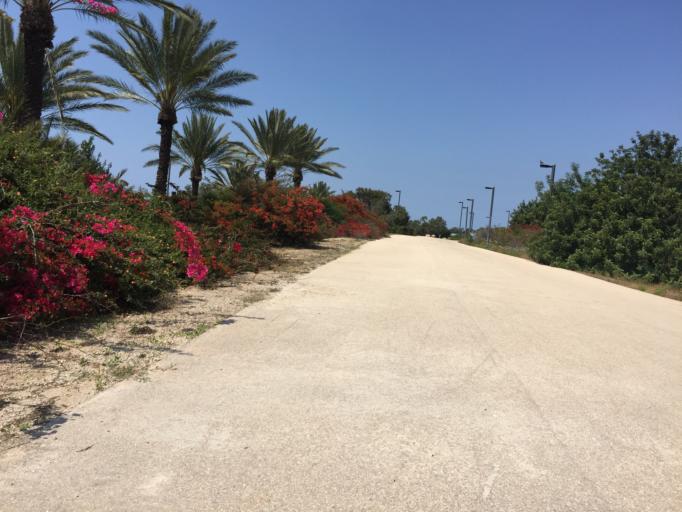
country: IL
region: Haifa
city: Qesarya
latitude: 32.4902
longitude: 34.9041
